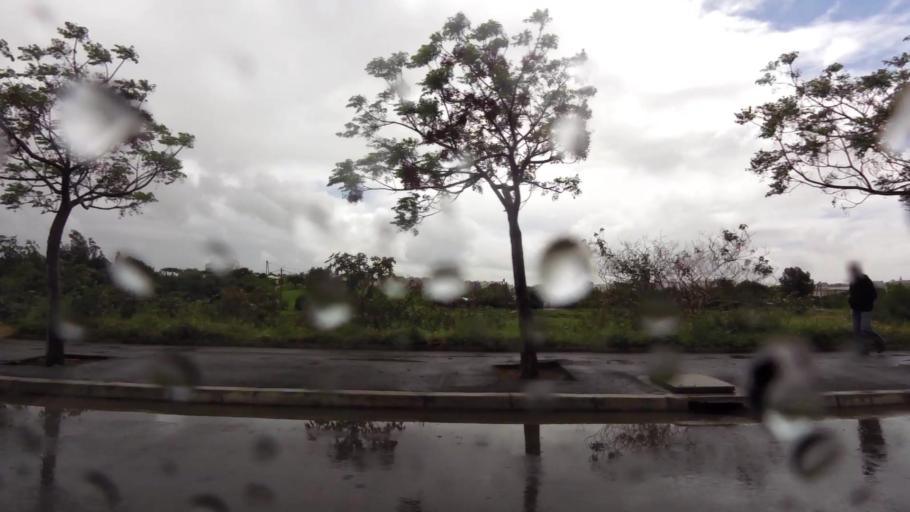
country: MA
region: Grand Casablanca
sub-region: Casablanca
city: Casablanca
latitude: 33.5347
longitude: -7.6571
